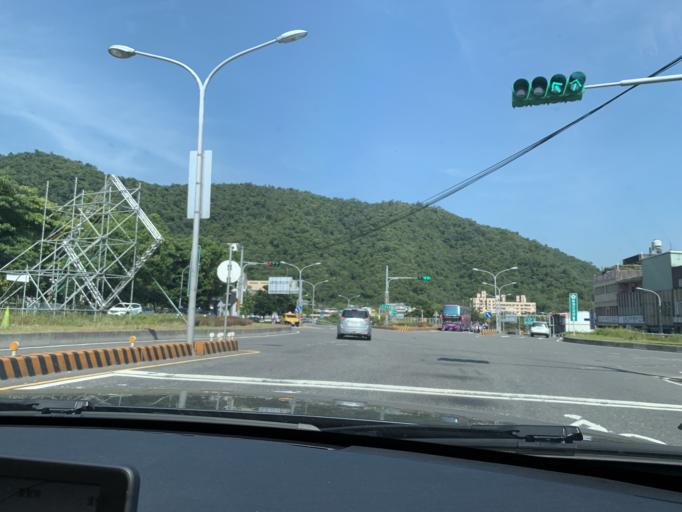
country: TW
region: Taiwan
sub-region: Yilan
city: Yilan
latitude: 24.5962
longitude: 121.8366
